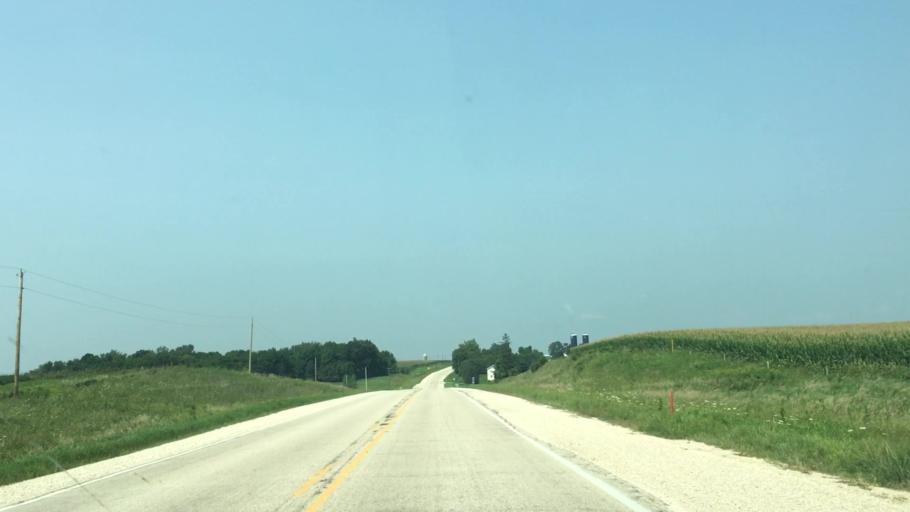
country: US
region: Iowa
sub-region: Fayette County
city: West Union
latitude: 43.0002
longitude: -91.8242
